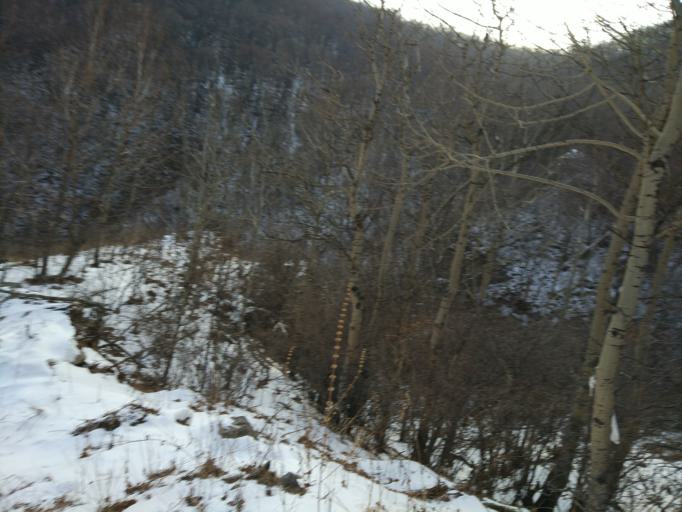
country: CN
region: Hebei
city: Xiwanzi
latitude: 40.8427
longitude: 115.4606
